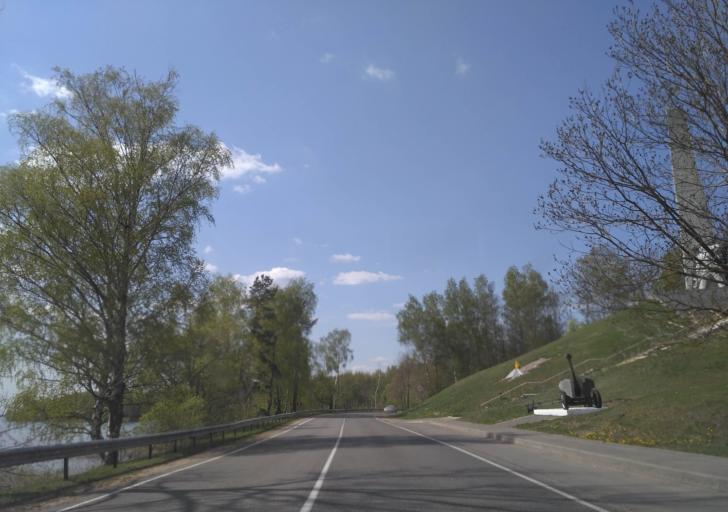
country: BY
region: Minsk
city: Myadzyel
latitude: 54.8851
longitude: 26.8375
